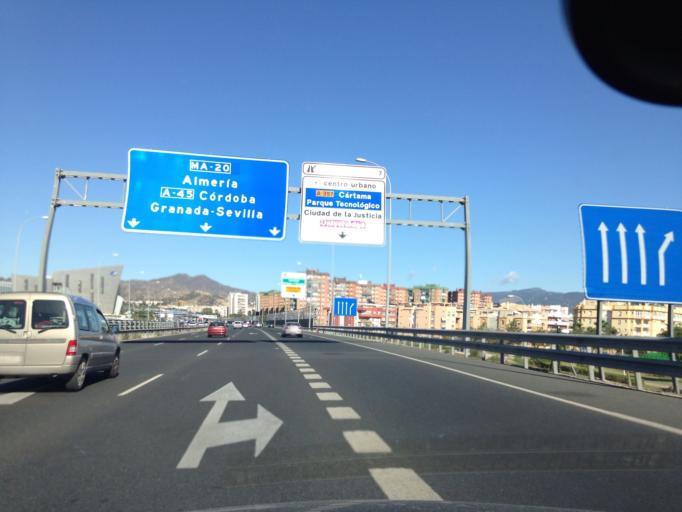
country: ES
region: Andalusia
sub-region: Provincia de Malaga
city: Malaga
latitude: 36.6981
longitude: -4.4587
